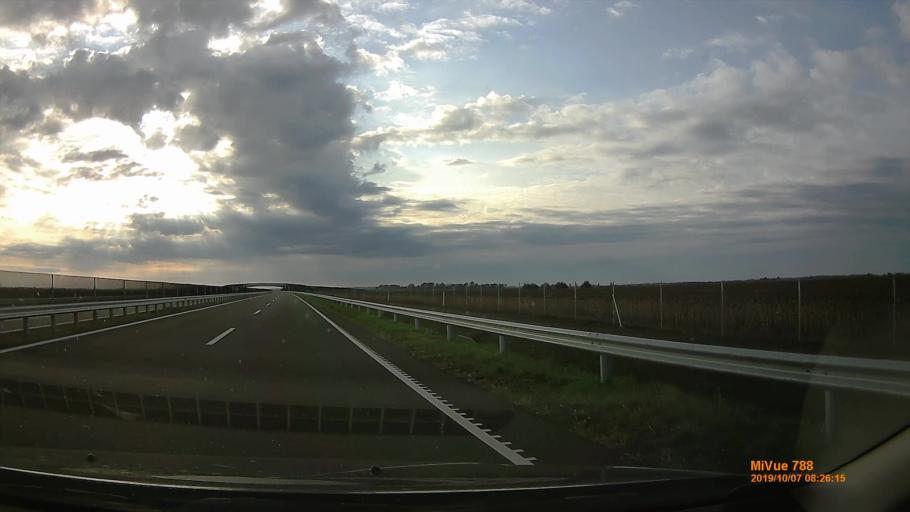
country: HU
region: Jasz-Nagykun-Szolnok
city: Kunszentmarton
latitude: 46.8230
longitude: 20.3671
